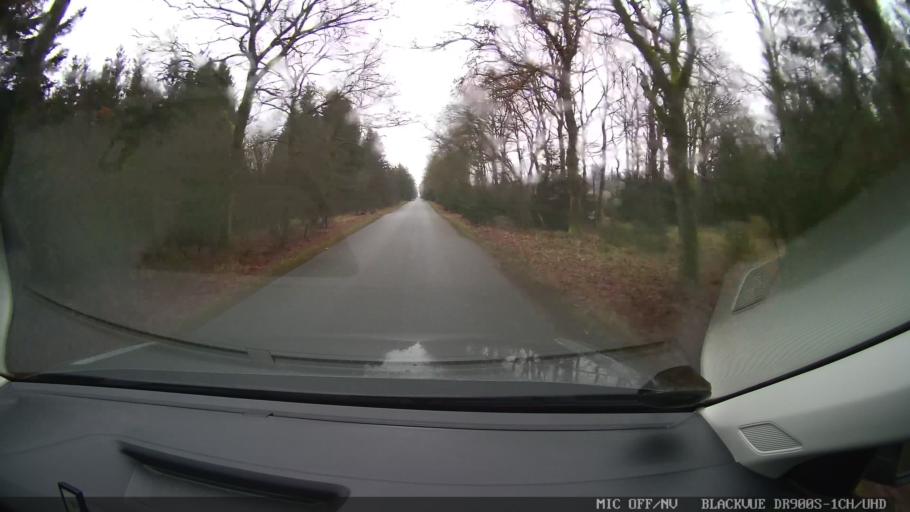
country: DK
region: Central Jutland
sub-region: Viborg Kommune
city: Karup
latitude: 56.2353
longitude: 9.1221
